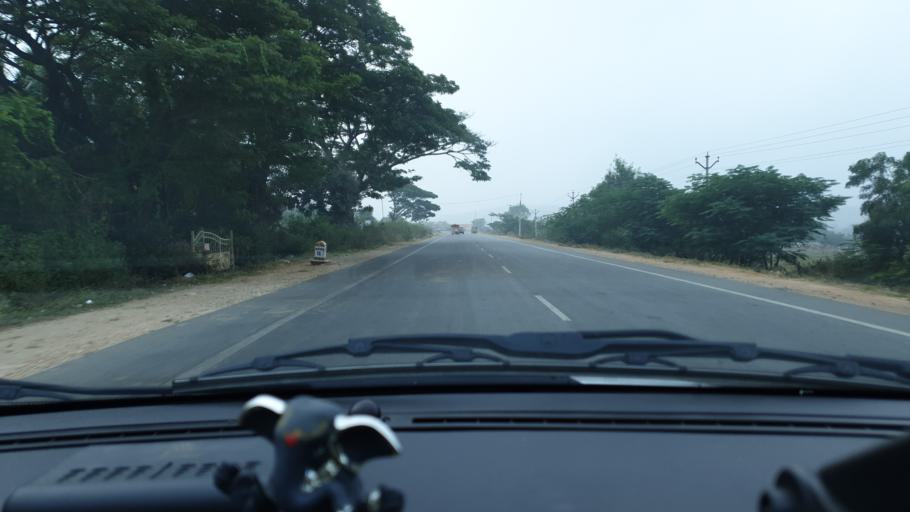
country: IN
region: Telangana
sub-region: Mahbubnagar
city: Farrukhnagar
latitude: 16.9600
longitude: 78.5124
